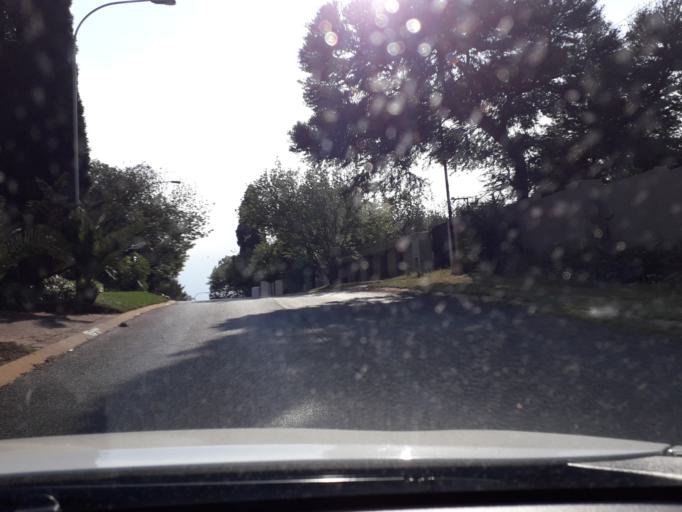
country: ZA
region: Gauteng
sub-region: City of Johannesburg Metropolitan Municipality
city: Roodepoort
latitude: -26.1553
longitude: 27.9574
